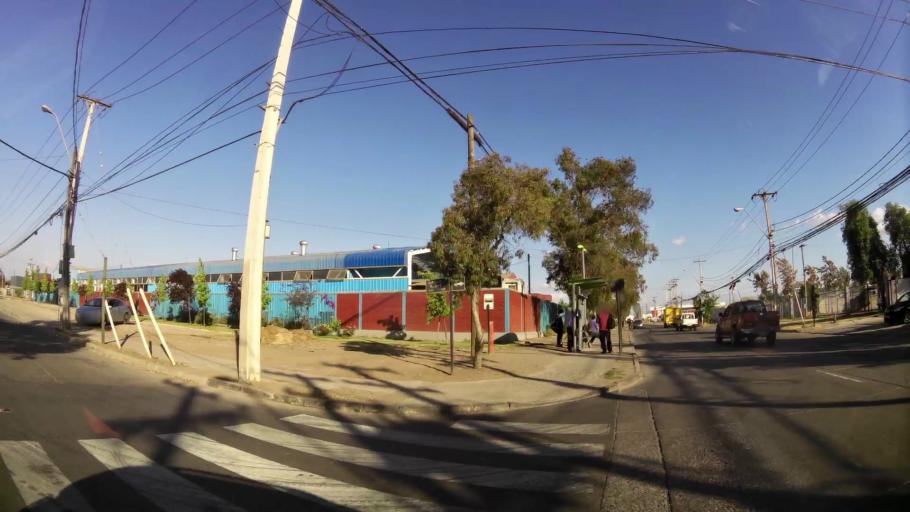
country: CL
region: Santiago Metropolitan
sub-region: Provincia de Maipo
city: San Bernardo
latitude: -33.5376
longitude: -70.7468
